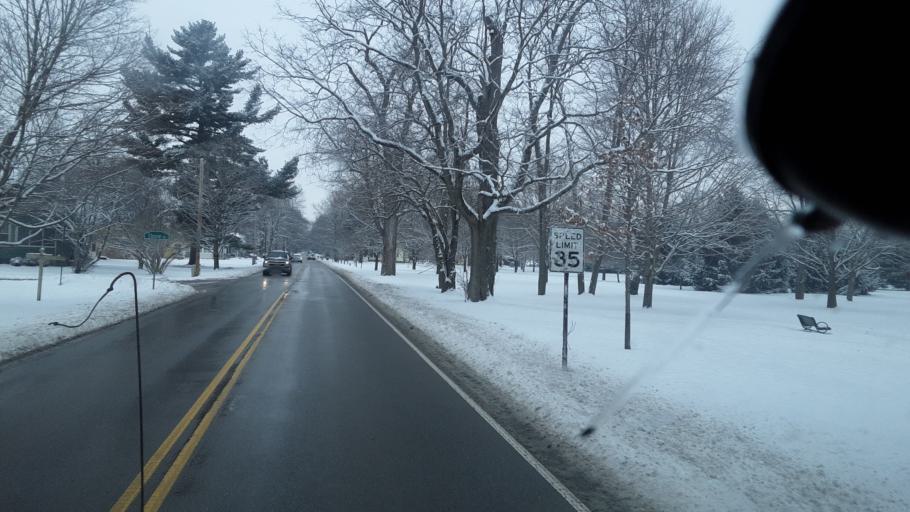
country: US
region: Ohio
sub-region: Licking County
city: Granville
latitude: 40.0640
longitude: -82.4950
